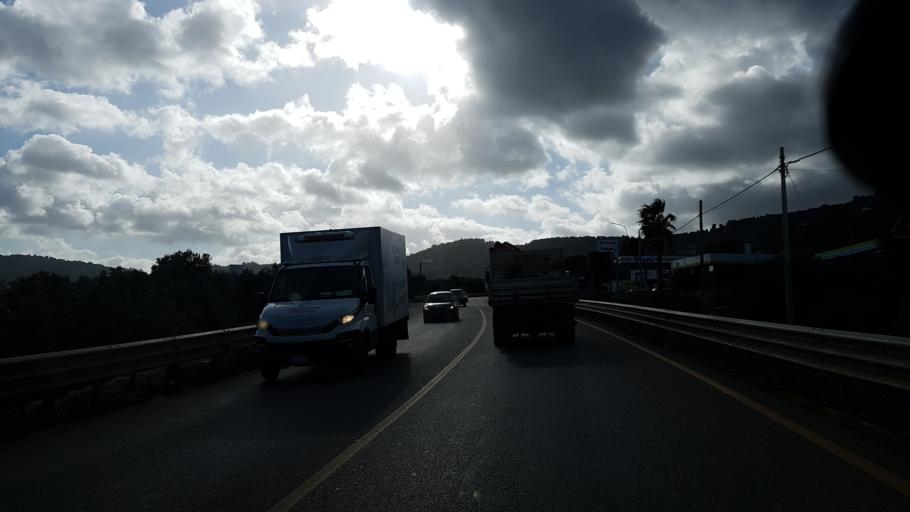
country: IT
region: Apulia
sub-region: Provincia di Brindisi
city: Fasano
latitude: 40.8258
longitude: 17.3496
